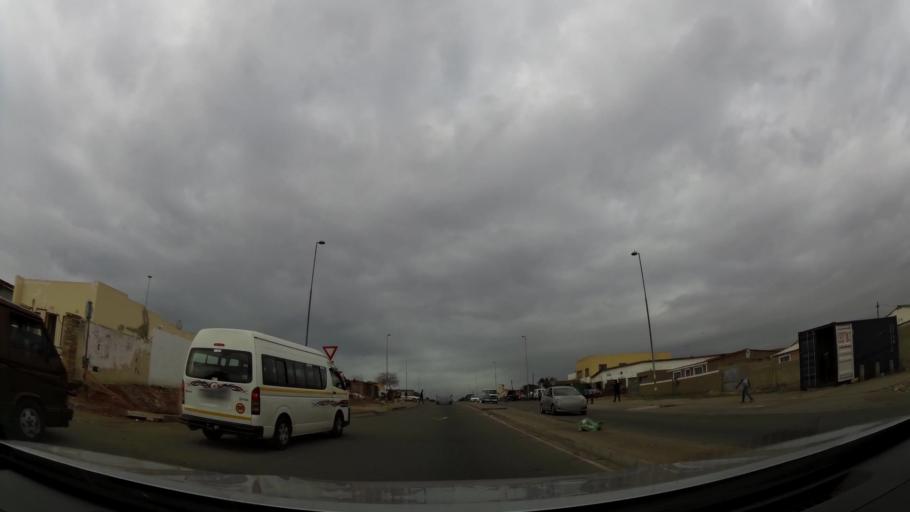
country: ZA
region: Eastern Cape
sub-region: Nelson Mandela Bay Metropolitan Municipality
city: Port Elizabeth
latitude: -33.8867
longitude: 25.5854
